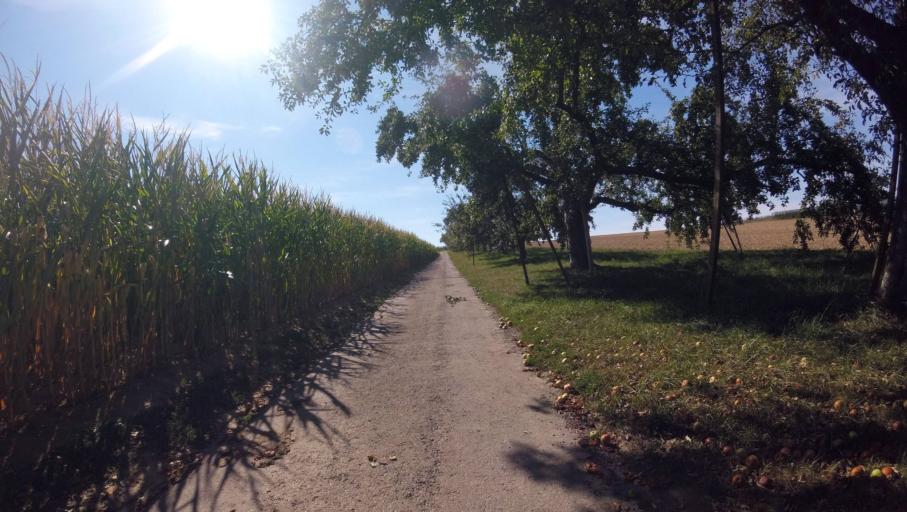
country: DE
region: Baden-Wuerttemberg
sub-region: Regierungsbezirk Stuttgart
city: Mittelschontal
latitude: 48.9409
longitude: 9.3947
